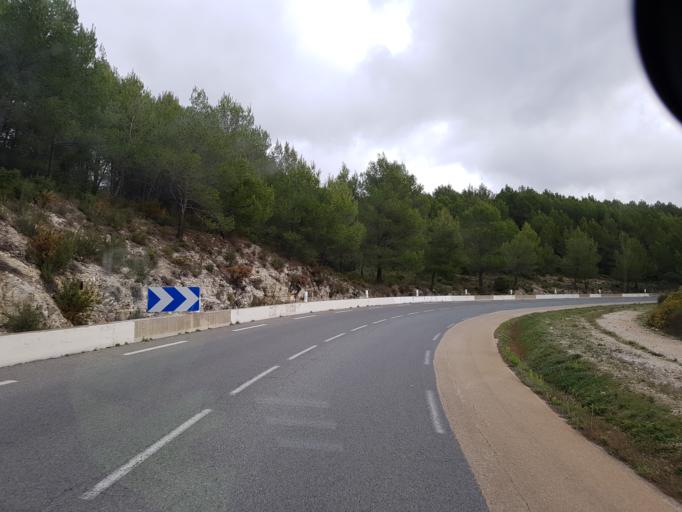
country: FR
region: Provence-Alpes-Cote d'Azur
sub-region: Departement des Bouches-du-Rhone
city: Cuges-les-Pins
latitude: 43.2658
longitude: 5.7480
